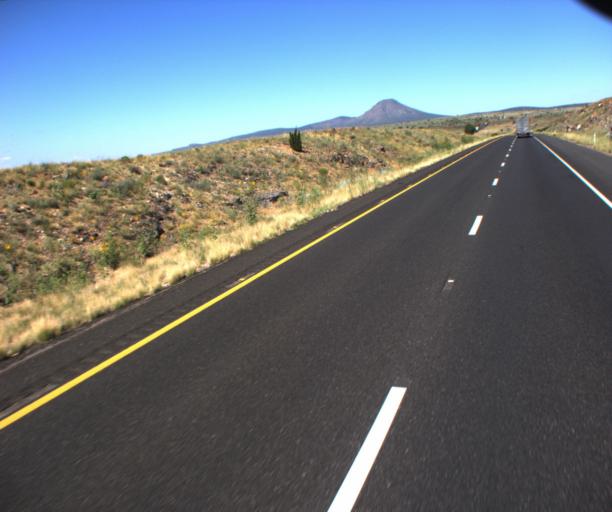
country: US
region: Arizona
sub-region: Yavapai County
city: Paulden
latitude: 35.2352
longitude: -112.6307
